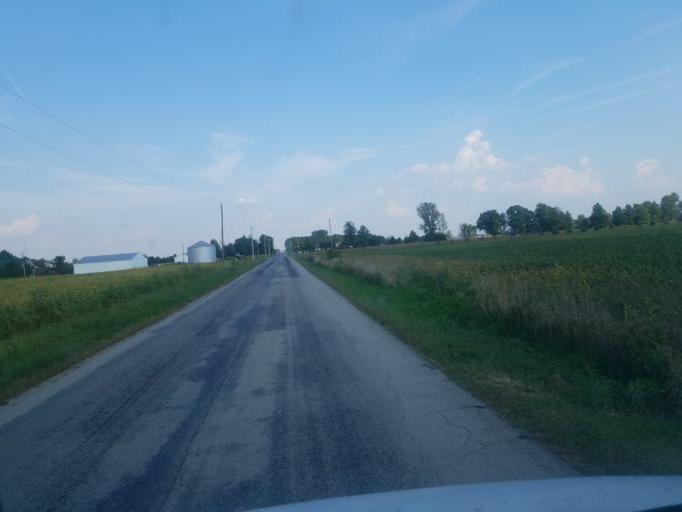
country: US
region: Ohio
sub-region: Wyandot County
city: Carey
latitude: 40.9050
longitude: -83.4691
